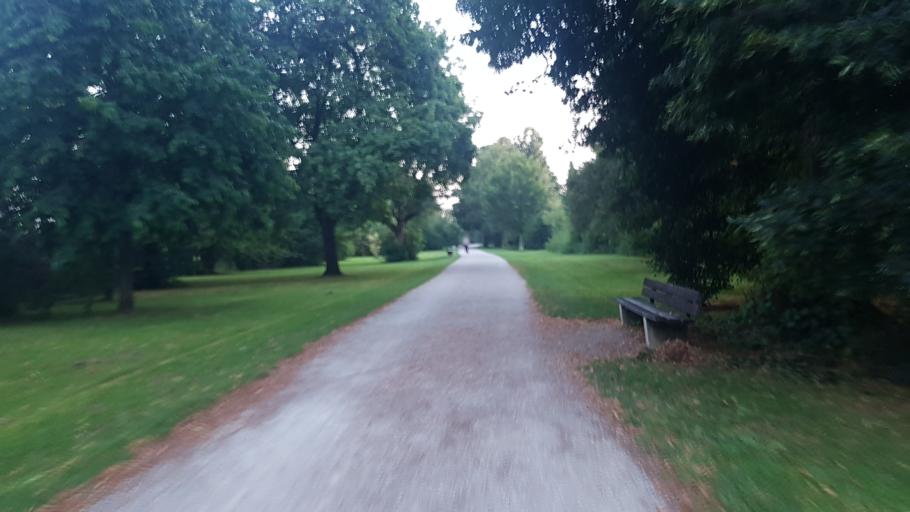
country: DE
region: Bavaria
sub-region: Upper Bavaria
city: Pasing
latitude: 48.1380
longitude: 11.4671
